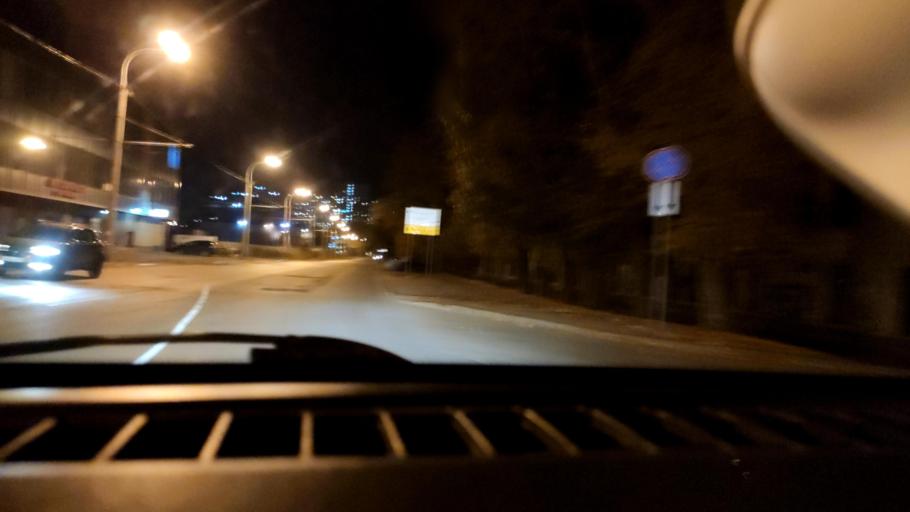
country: RU
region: Samara
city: Samara
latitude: 53.2123
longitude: 50.1886
